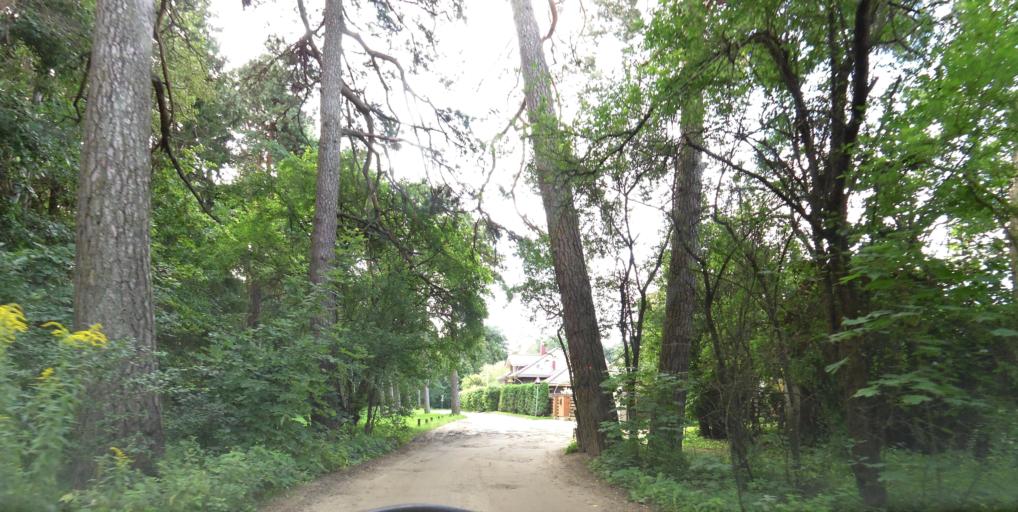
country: LT
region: Vilnius County
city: Seskine
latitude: 54.7342
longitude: 25.2844
